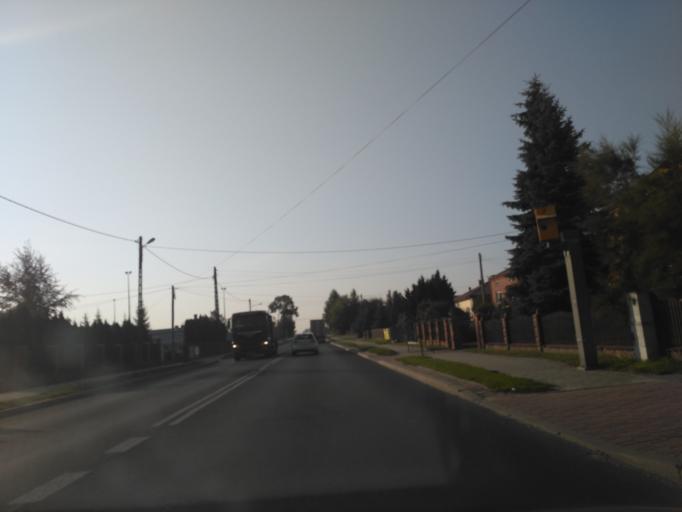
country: PL
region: Lublin Voivodeship
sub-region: Powiat janowski
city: Modliborzyce
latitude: 50.7509
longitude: 22.3348
